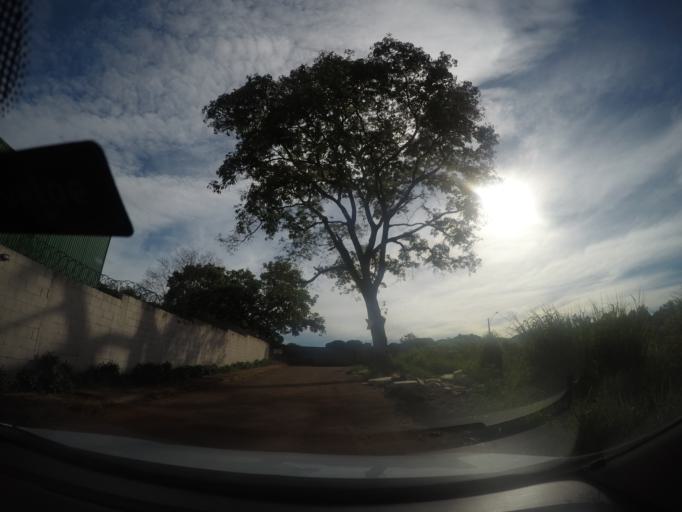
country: BR
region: Goias
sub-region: Goiania
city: Goiania
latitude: -16.6335
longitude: -49.3492
